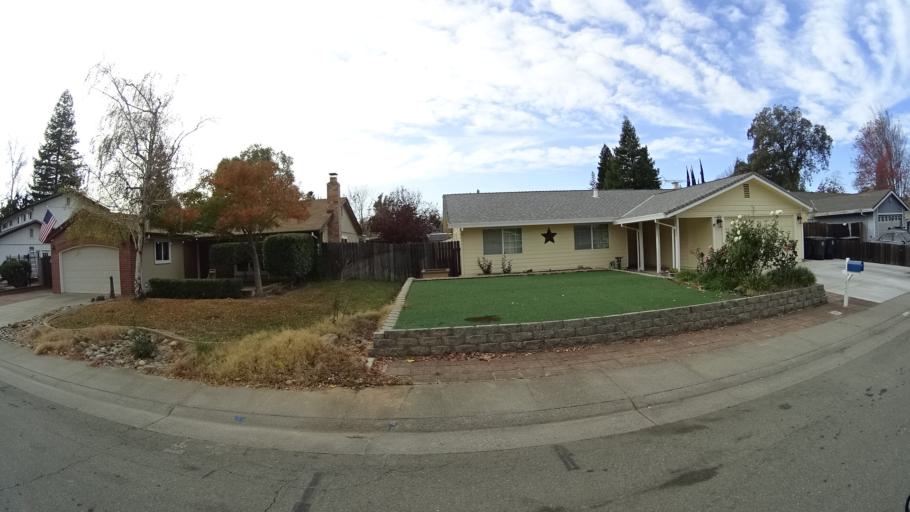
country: US
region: California
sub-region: Sacramento County
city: Citrus Heights
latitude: 38.7087
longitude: -121.2499
